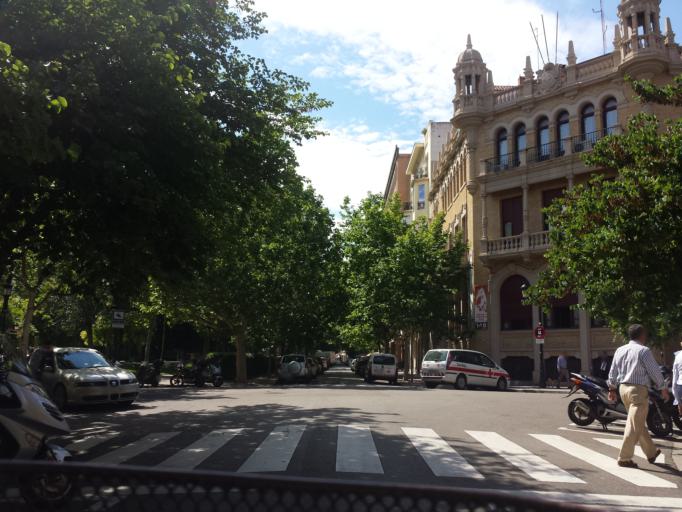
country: ES
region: Aragon
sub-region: Provincia de Zaragoza
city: Zaragoza
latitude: 41.6492
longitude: -0.8781
